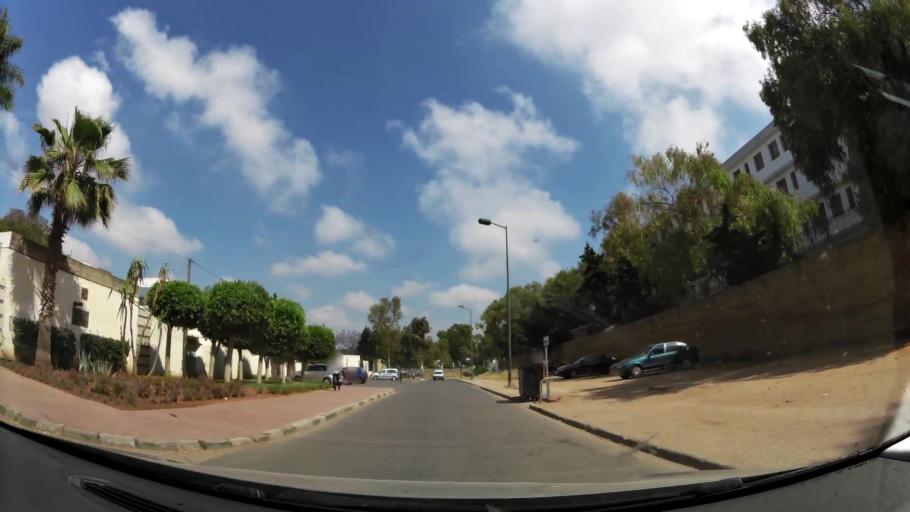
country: MA
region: Rabat-Sale-Zemmour-Zaer
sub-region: Rabat
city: Rabat
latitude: 33.9867
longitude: -6.8586
